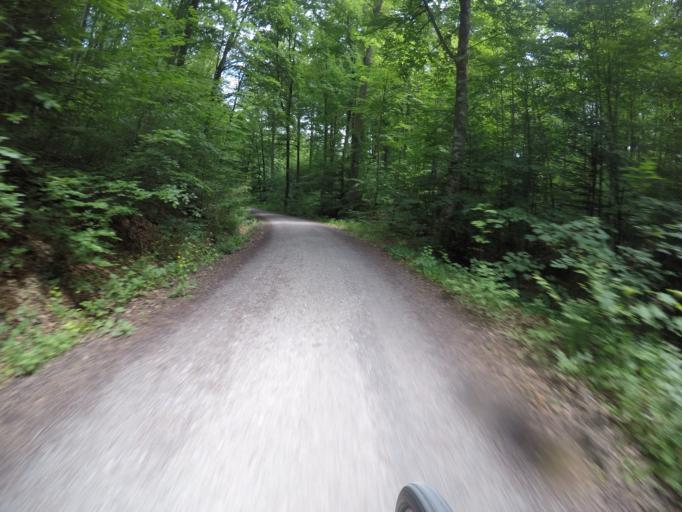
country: DE
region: Baden-Wuerttemberg
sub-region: Regierungsbezirk Stuttgart
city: Nufringen
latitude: 48.5975
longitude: 8.9151
